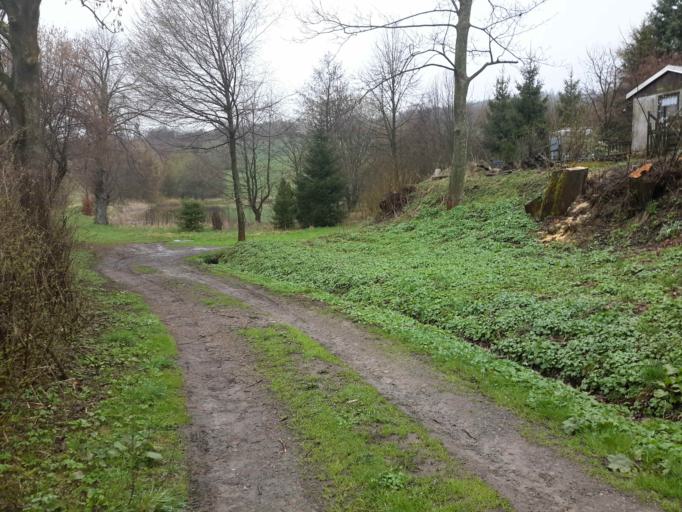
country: DE
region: Saxony
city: Sayda
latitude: 50.7170
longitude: 13.4183
